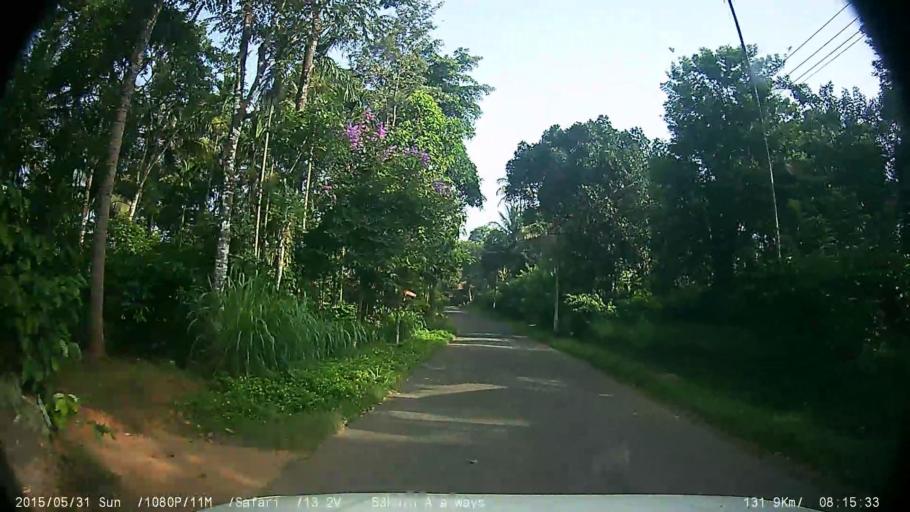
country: IN
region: Kerala
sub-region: Wayanad
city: Kalpetta
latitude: 11.6506
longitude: 76.0022
